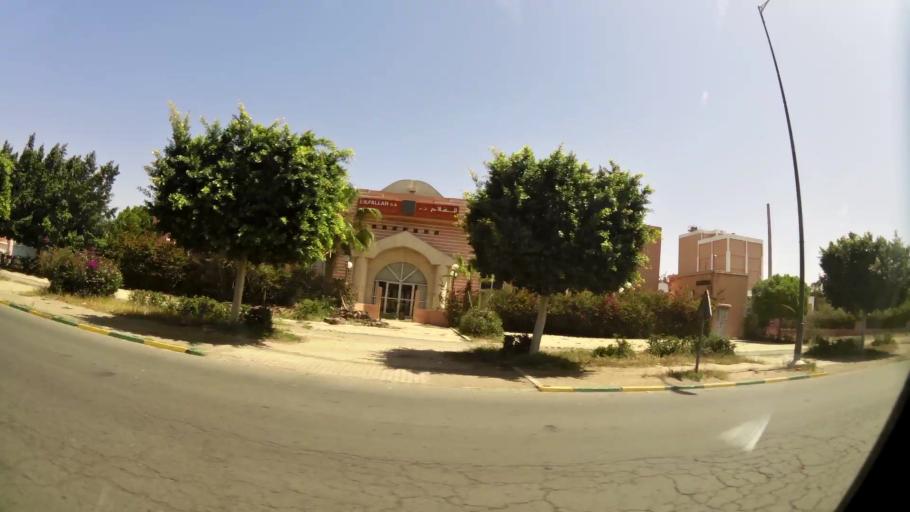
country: MA
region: Souss-Massa-Draa
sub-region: Inezgane-Ait Mellou
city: Inezgane
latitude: 30.3340
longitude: -9.4912
